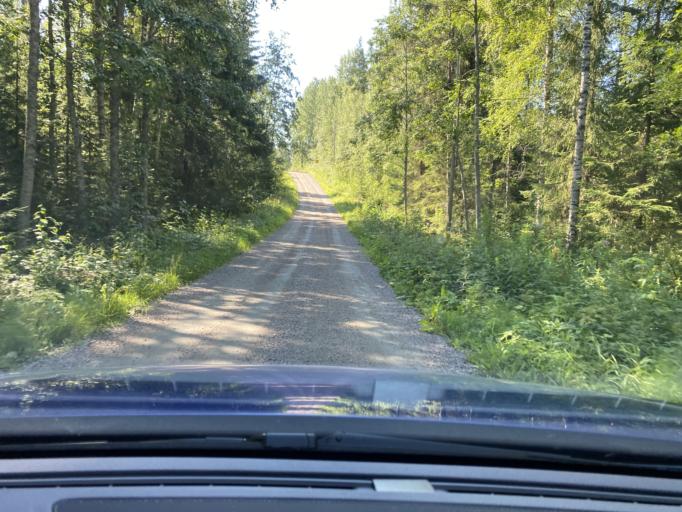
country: FI
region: Central Finland
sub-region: Jaemsae
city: Jaemsae
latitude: 61.8601
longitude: 25.3947
